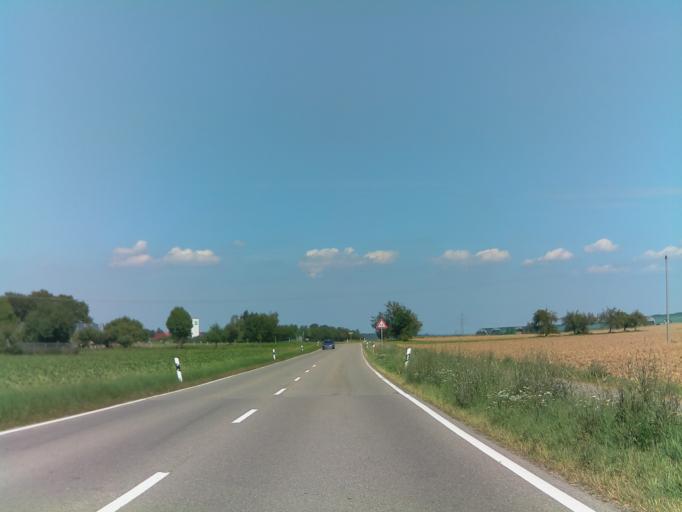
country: DE
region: Baden-Wuerttemberg
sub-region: Regierungsbezirk Stuttgart
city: Rutesheim
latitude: 48.8389
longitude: 8.9747
